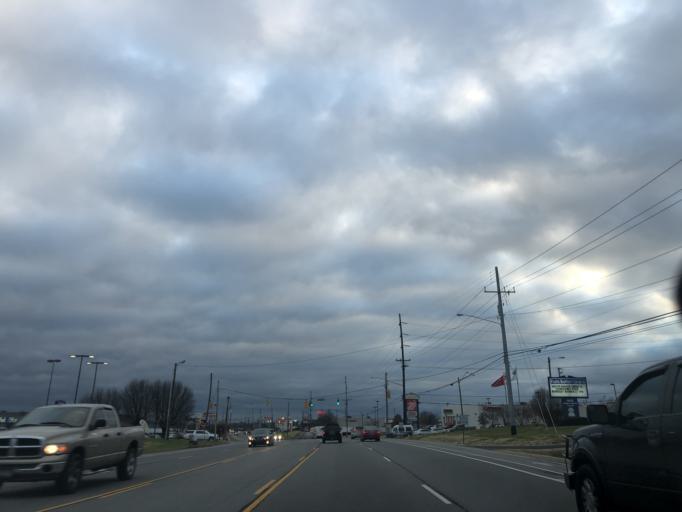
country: US
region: Tennessee
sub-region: Davidson County
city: Goodlettsville
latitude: 36.2941
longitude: -86.7017
